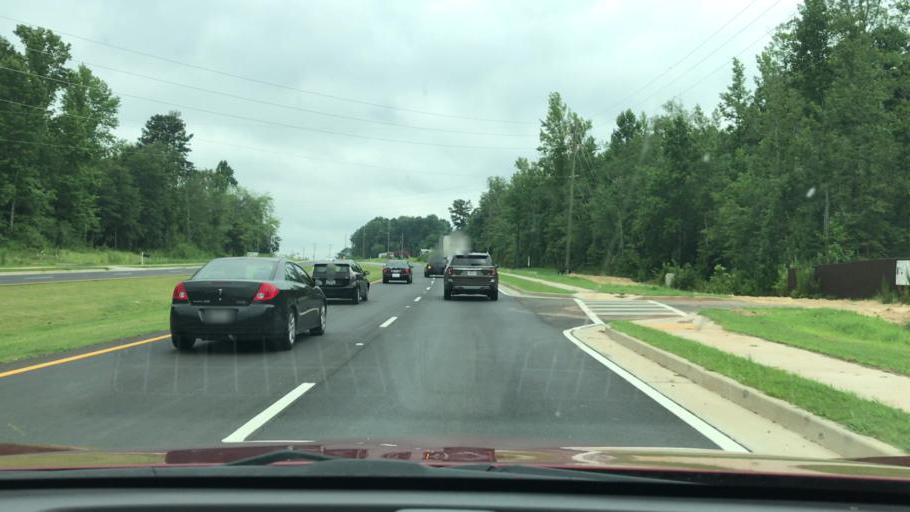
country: US
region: Georgia
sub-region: Forsyth County
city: Cumming
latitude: 34.1541
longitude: -84.1062
